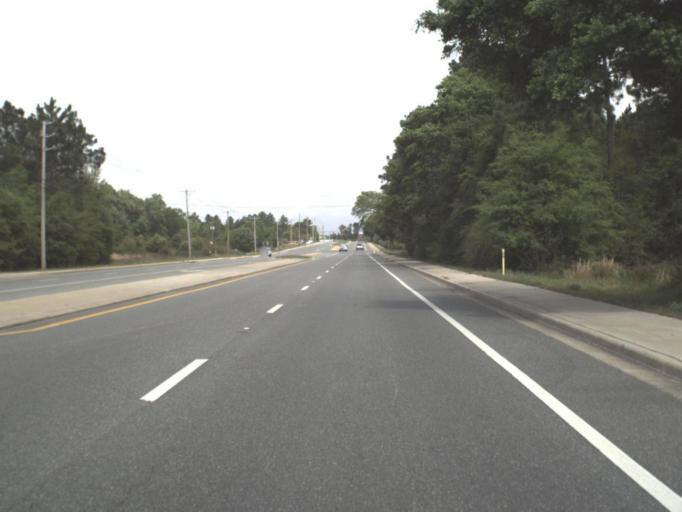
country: US
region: Florida
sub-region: Santa Rosa County
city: East Milton
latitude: 30.6273
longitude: -86.9676
